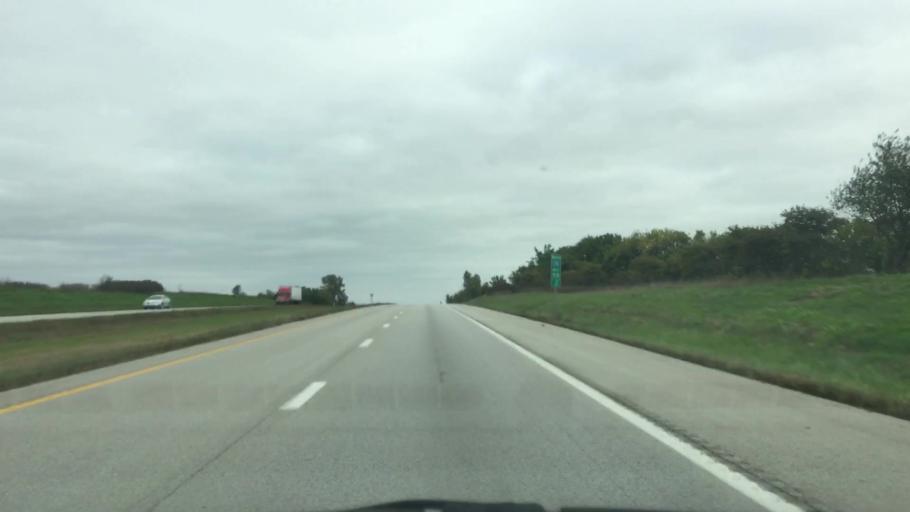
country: US
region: Missouri
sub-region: Clinton County
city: Cameron
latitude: 39.8082
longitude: -94.1967
